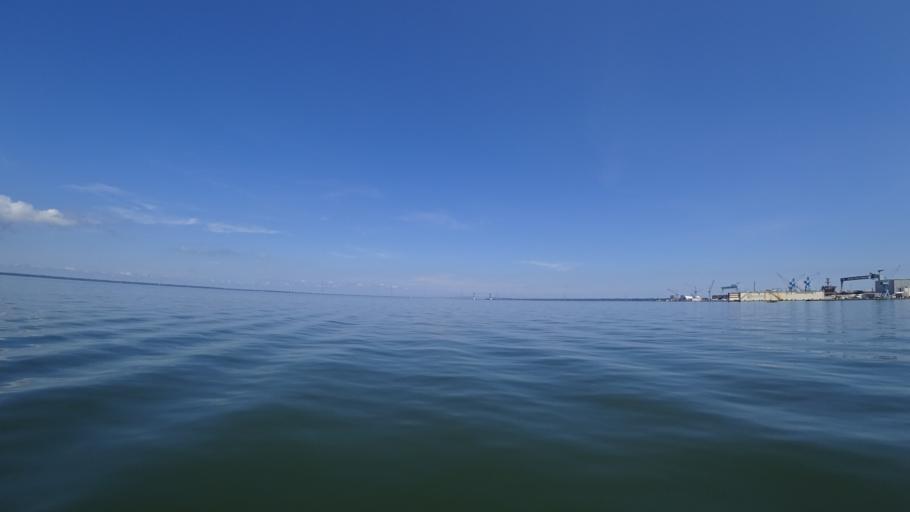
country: US
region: Virginia
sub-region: City of Newport News
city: Newport News
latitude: 36.9810
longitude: -76.4478
